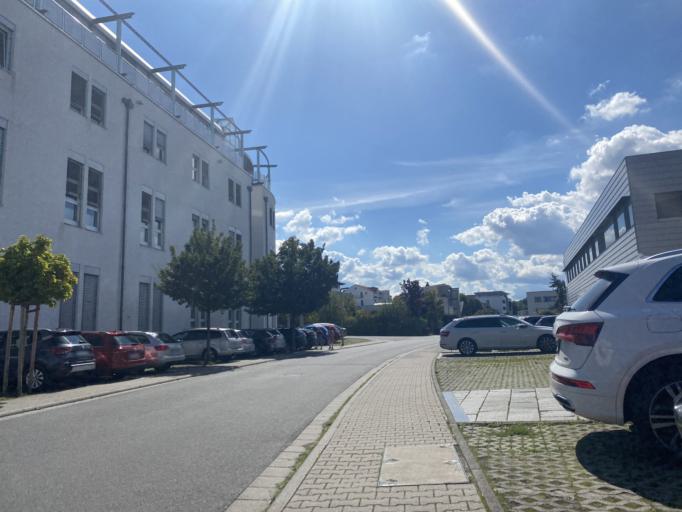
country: DE
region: Hesse
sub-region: Regierungsbezirk Darmstadt
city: Rossdorf
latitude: 49.8655
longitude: 8.7451
